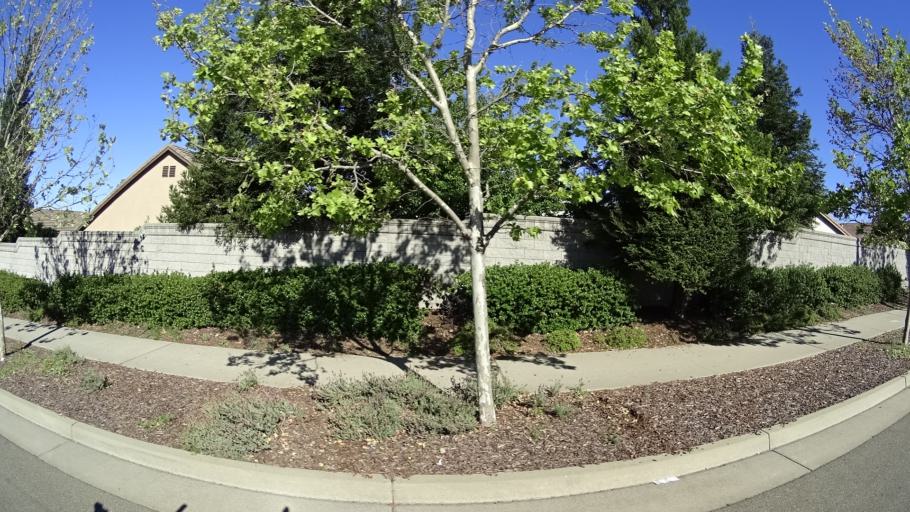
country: US
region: California
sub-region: Placer County
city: Rocklin
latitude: 38.8027
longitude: -121.2760
